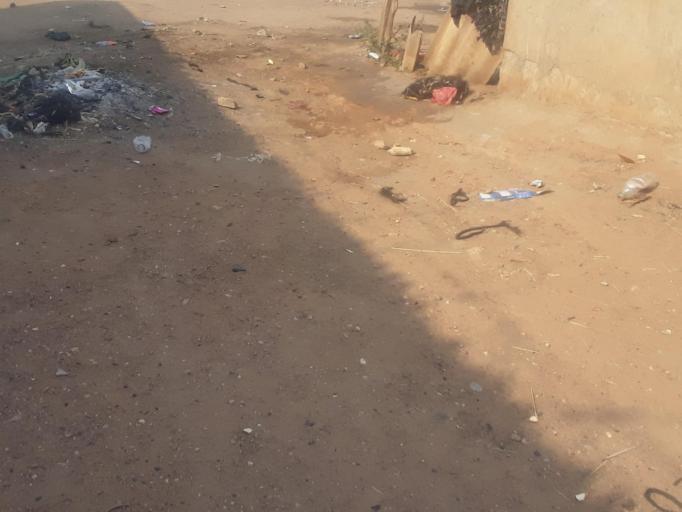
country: ZM
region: Lusaka
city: Lusaka
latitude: -15.3572
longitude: 28.2908
